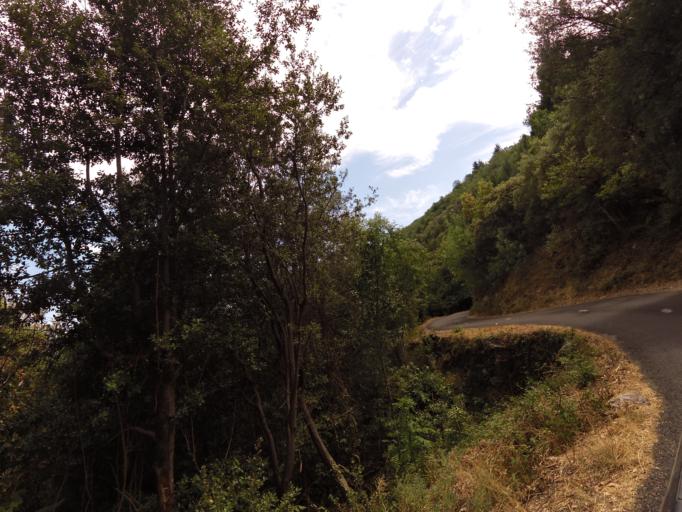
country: FR
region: Languedoc-Roussillon
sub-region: Departement du Gard
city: Le Vigan
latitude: 44.0193
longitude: 3.6352
